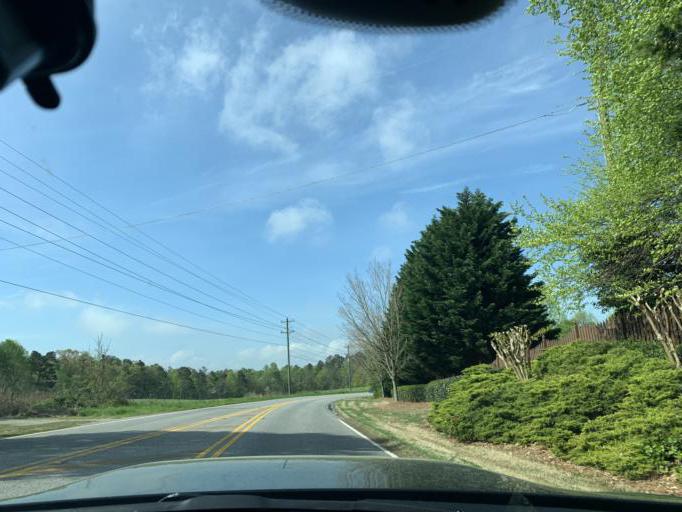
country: US
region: Georgia
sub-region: Forsyth County
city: Cumming
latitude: 34.2503
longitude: -84.0750
